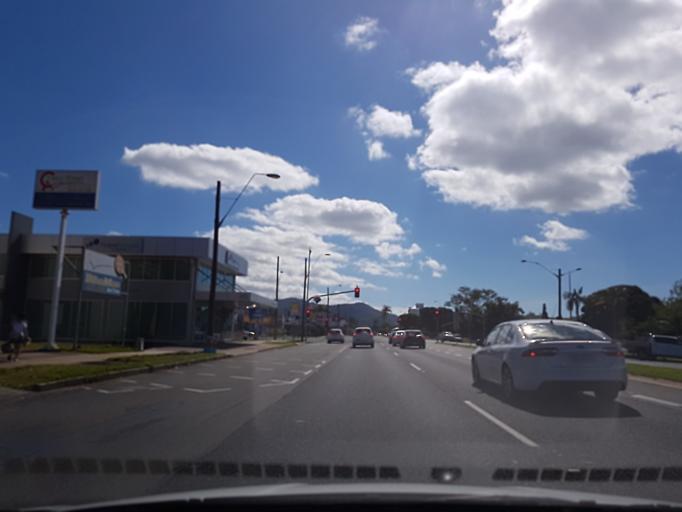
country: AU
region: Queensland
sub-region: Cairns
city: Cairns
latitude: -16.9210
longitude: 145.7713
